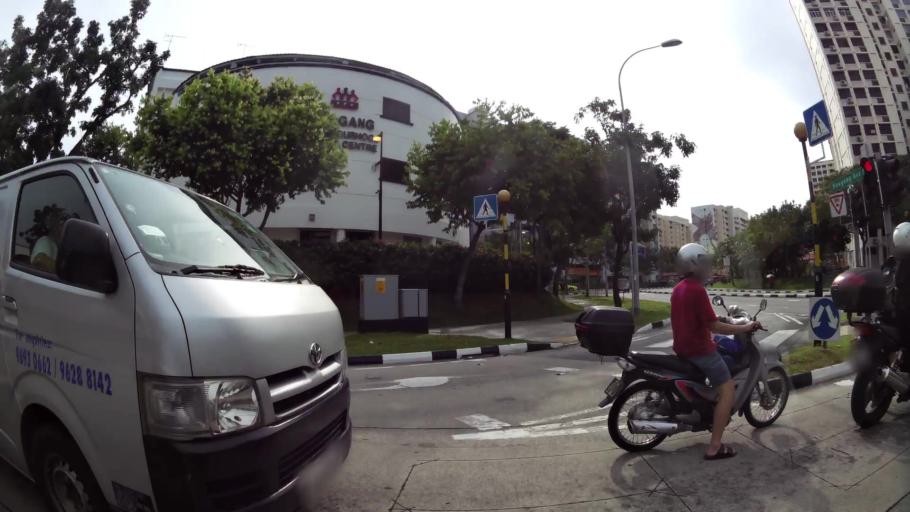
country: SG
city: Singapore
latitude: 1.3746
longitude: 103.8851
